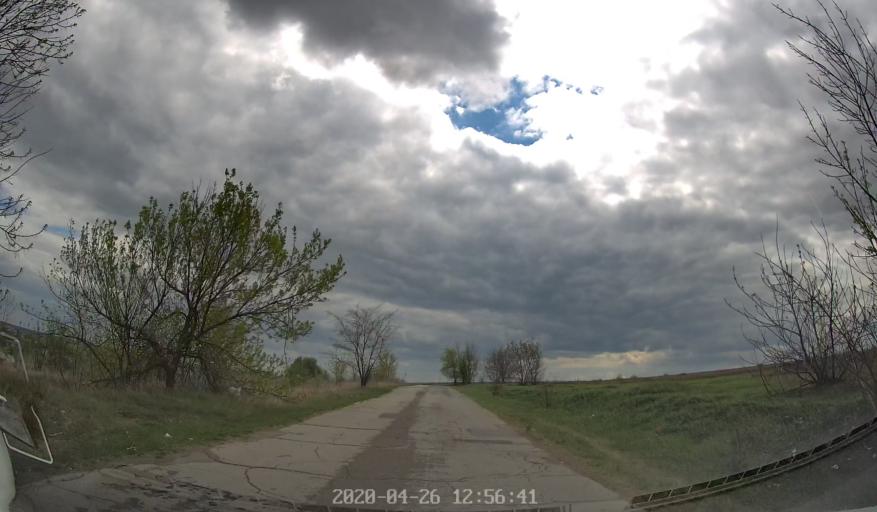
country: MD
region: Chisinau
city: Vadul lui Voda
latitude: 47.0712
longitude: 29.0671
